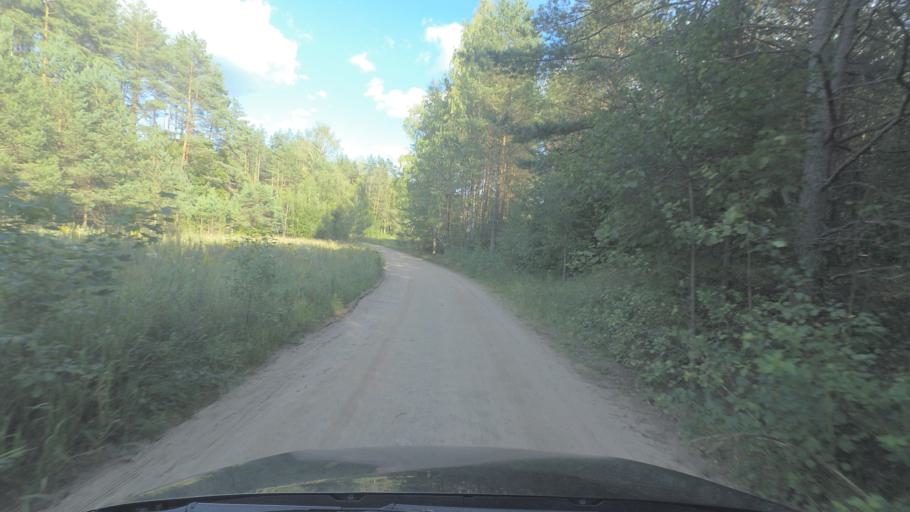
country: LT
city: Pabrade
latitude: 55.1397
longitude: 25.7227
